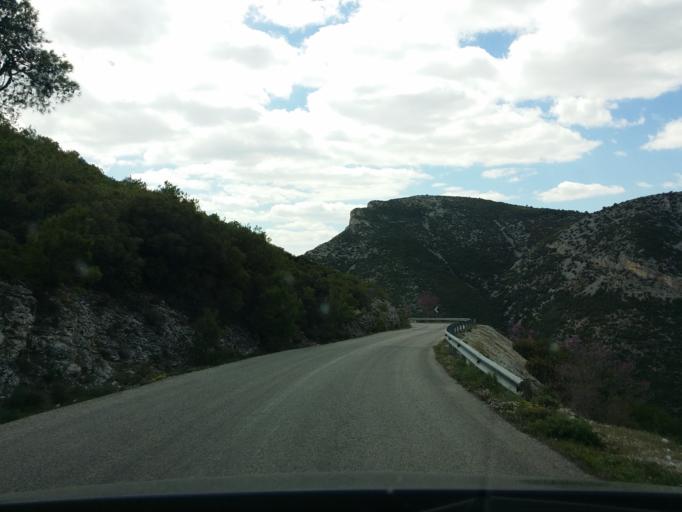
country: GR
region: Attica
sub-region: Nomarchia Dytikis Attikis
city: Fyli
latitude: 38.1162
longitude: 23.6468
